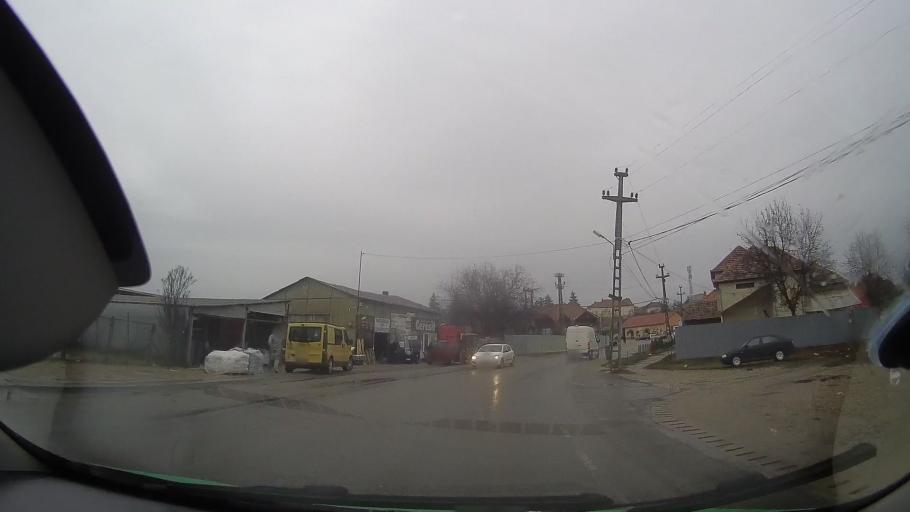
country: RO
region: Bihor
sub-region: Comuna Tinca
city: Tinca
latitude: 46.7714
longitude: 21.9305
